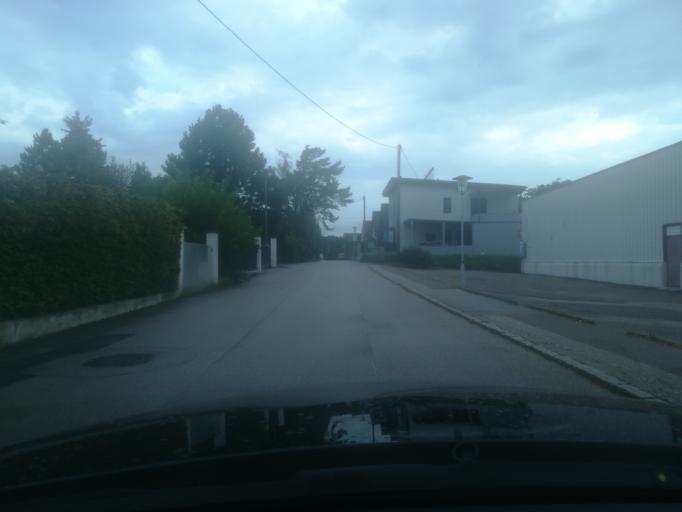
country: AT
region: Upper Austria
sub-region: Wels-Land
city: Marchtrenk
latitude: 48.1908
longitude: 14.1058
